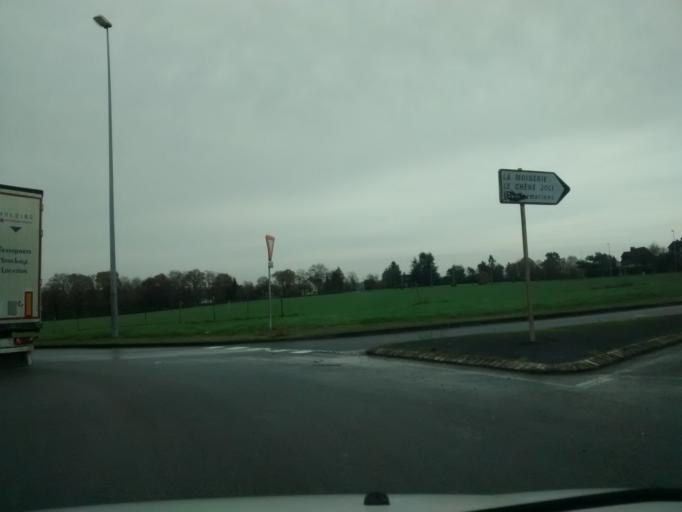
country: FR
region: Brittany
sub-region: Departement d'Ille-et-Vilaine
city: Acigne
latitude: 48.1229
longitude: -1.5304
